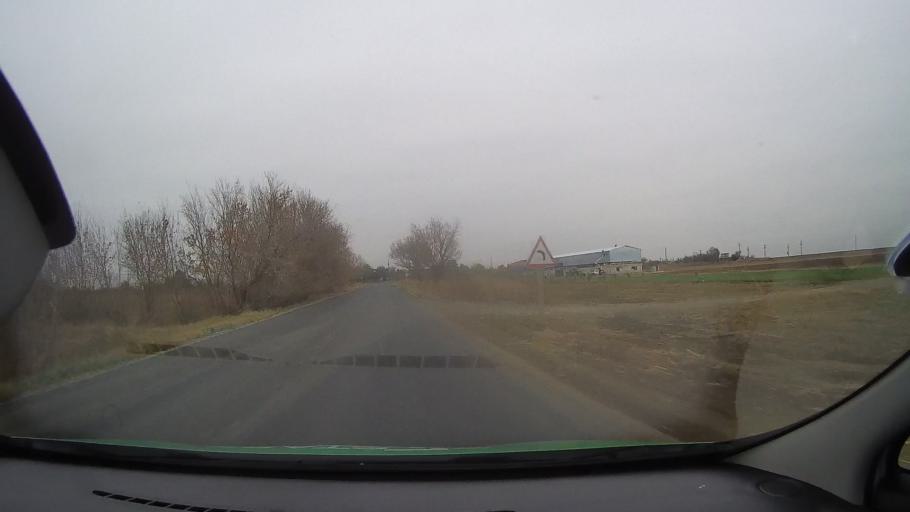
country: RO
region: Ialomita
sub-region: Comuna Valea Ciorii
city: Valea Ciorii
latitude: 44.7392
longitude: 27.5775
